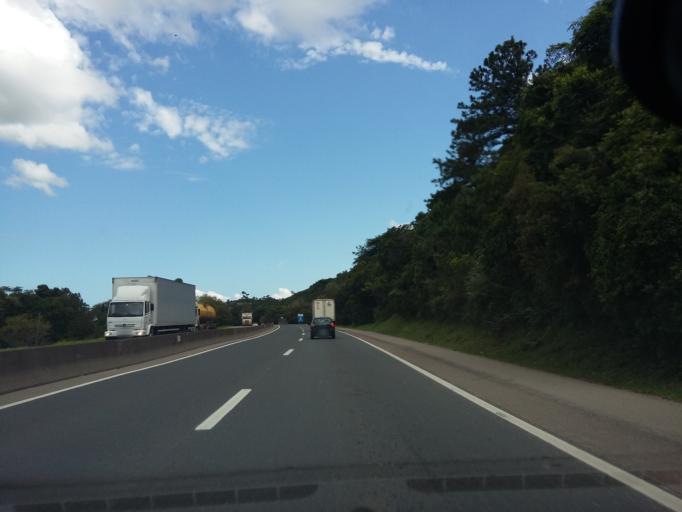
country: BR
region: Santa Catarina
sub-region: Tijucas
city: Tijucas
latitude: -27.3647
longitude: -48.6340
